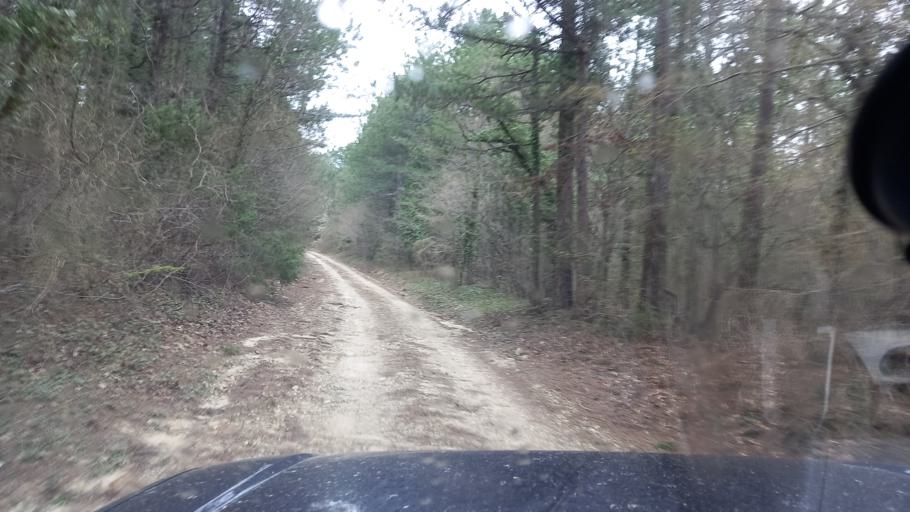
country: RU
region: Krasnodarskiy
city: Arkhipo-Osipovka
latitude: 44.3732
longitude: 38.4597
